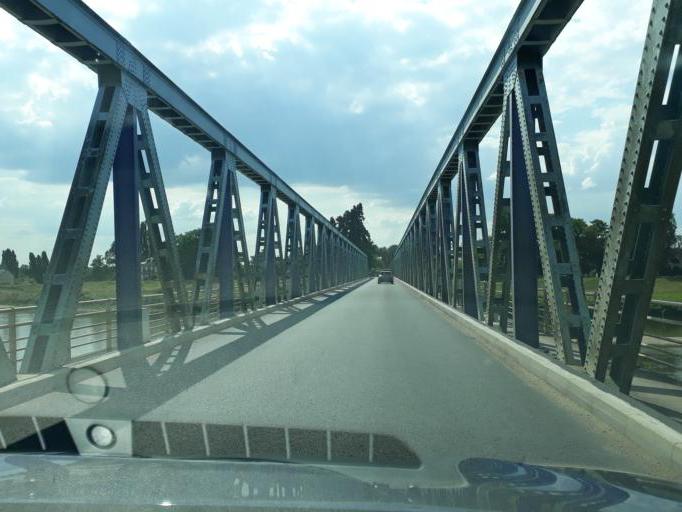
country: FR
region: Bourgogne
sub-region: Departement de la Nievre
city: Fourchambault
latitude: 47.0124
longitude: 3.0734
